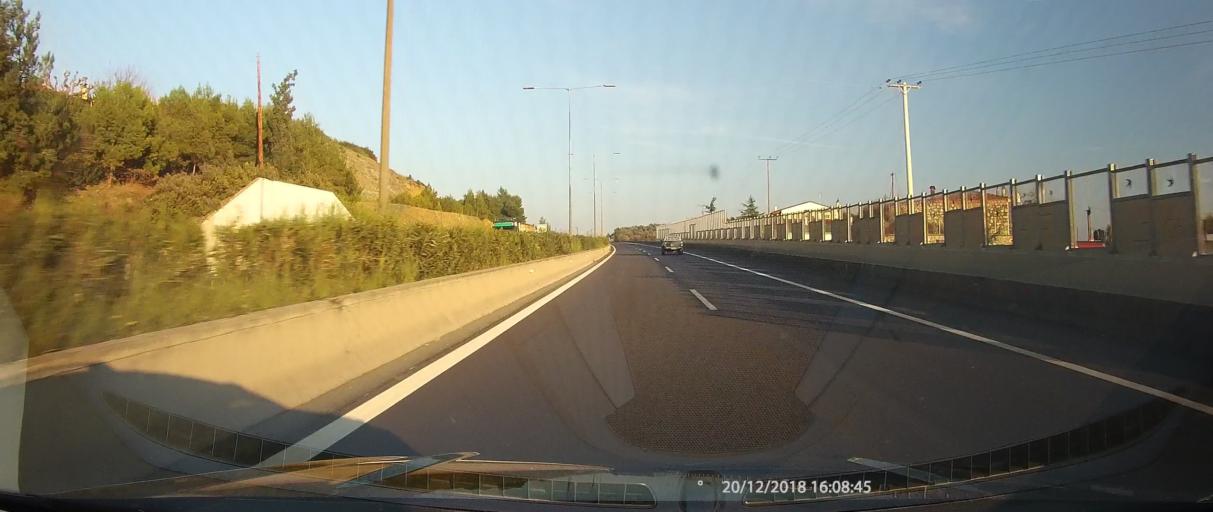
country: GR
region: Central Greece
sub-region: Nomos Fthiotidos
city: Pelasgia
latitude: 38.8844
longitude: 22.7731
